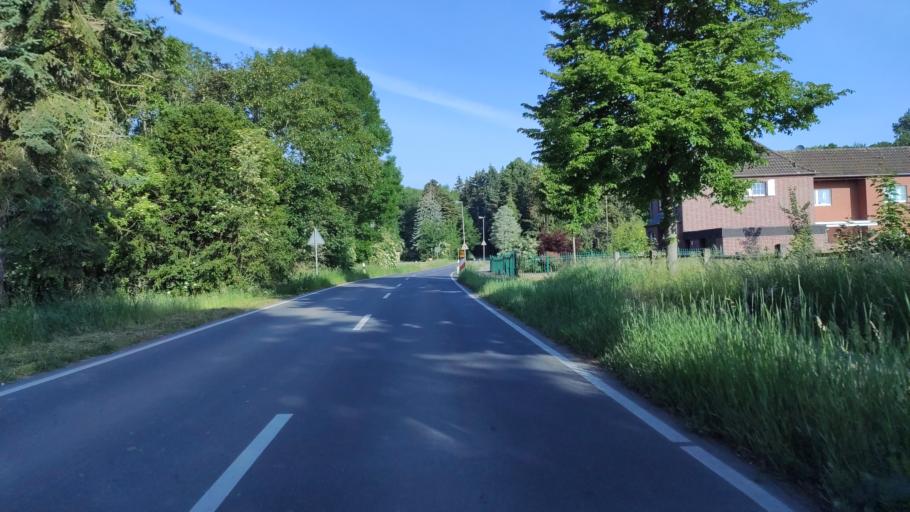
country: DE
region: North Rhine-Westphalia
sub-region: Regierungsbezirk Dusseldorf
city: Dormagen
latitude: 51.1104
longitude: 6.7476
